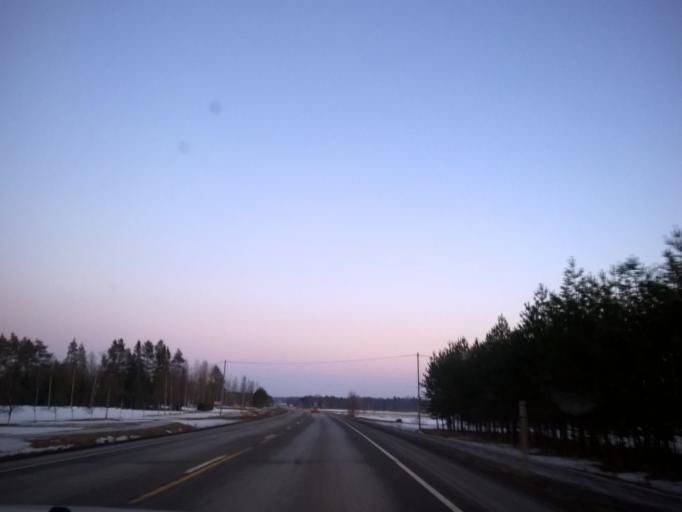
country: FI
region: Northern Ostrobothnia
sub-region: Nivala-Haapajaervi
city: Kaersaemaeki
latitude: 63.8488
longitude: 25.8481
